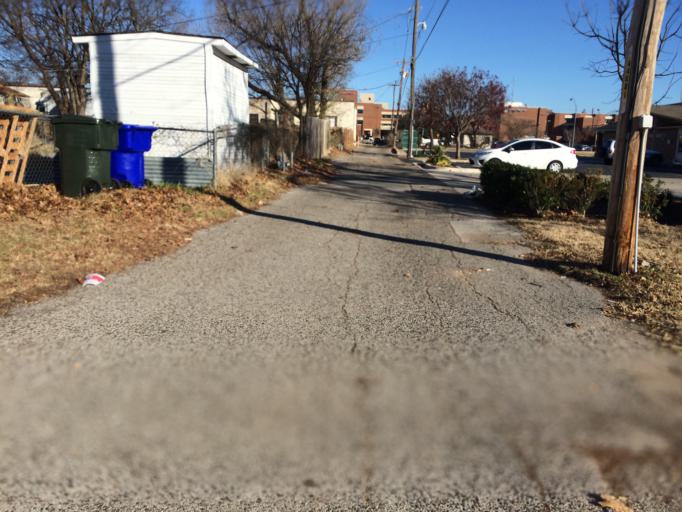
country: US
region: Oklahoma
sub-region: Cleveland County
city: Norman
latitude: 35.2310
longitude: -97.4426
